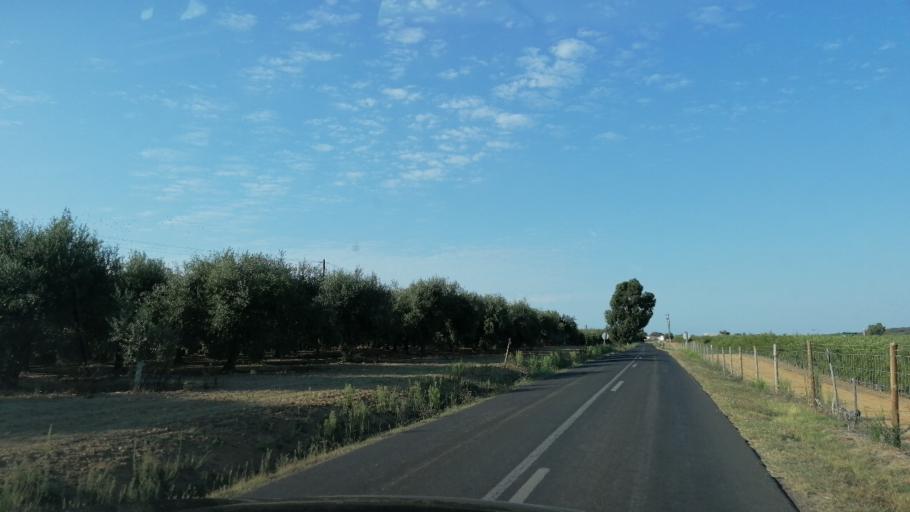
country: PT
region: Santarem
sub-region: Santarem
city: Santarem
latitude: 39.2761
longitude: -8.6605
